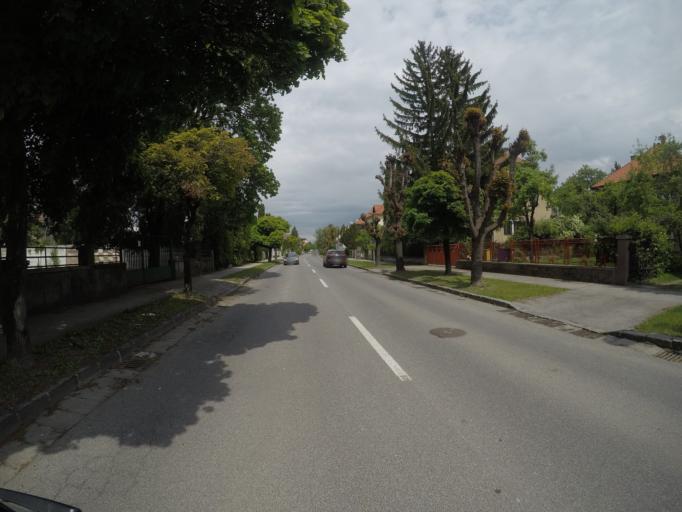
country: SK
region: Banskobystricky
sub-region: Okres Banska Bystrica
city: Zvolen
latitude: 48.5747
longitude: 19.1215
